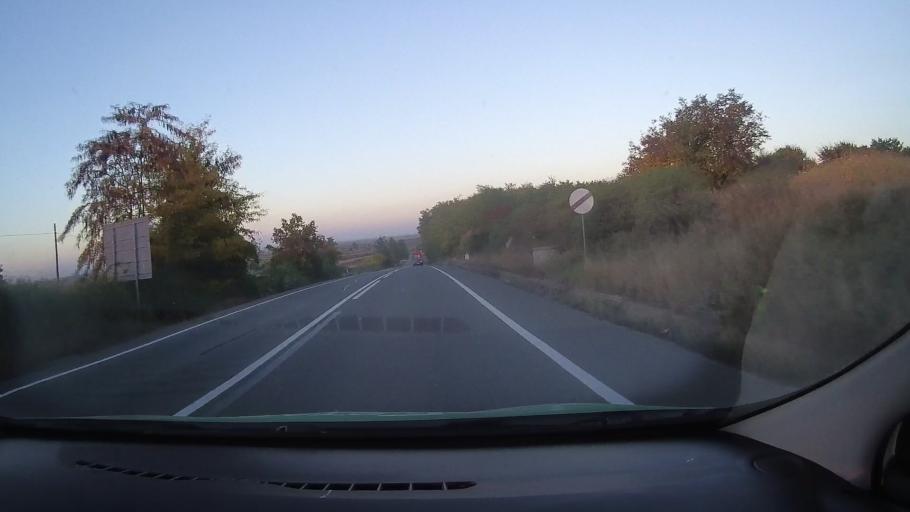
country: RO
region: Bihor
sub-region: Comuna Cherechiu
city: Cherechiu
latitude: 47.3788
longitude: 22.1397
